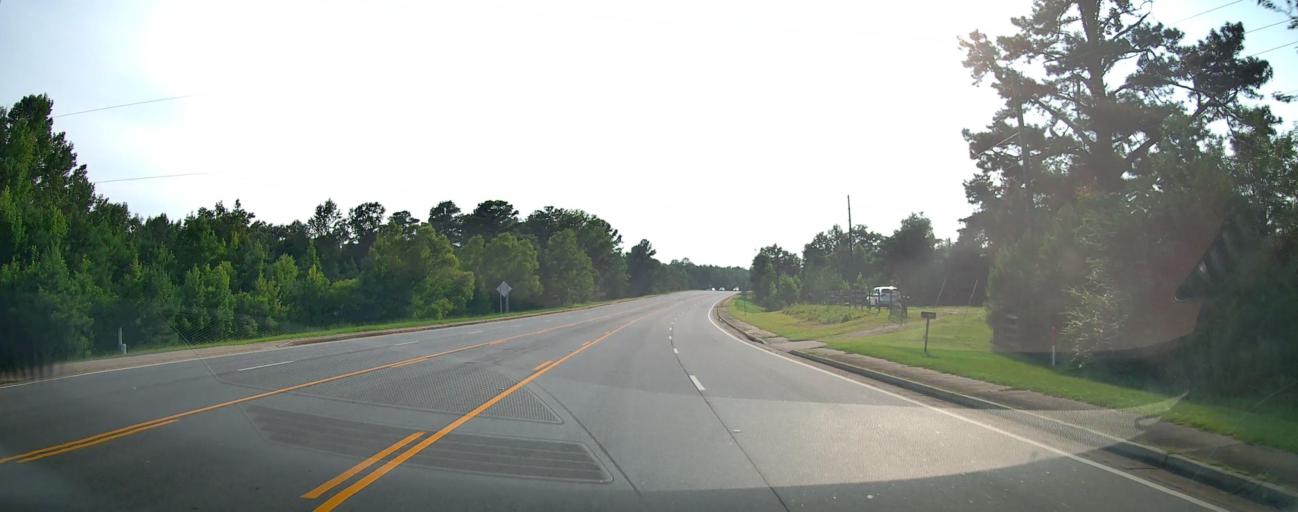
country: US
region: Georgia
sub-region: Talbot County
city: Talbotton
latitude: 32.5751
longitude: -84.5612
